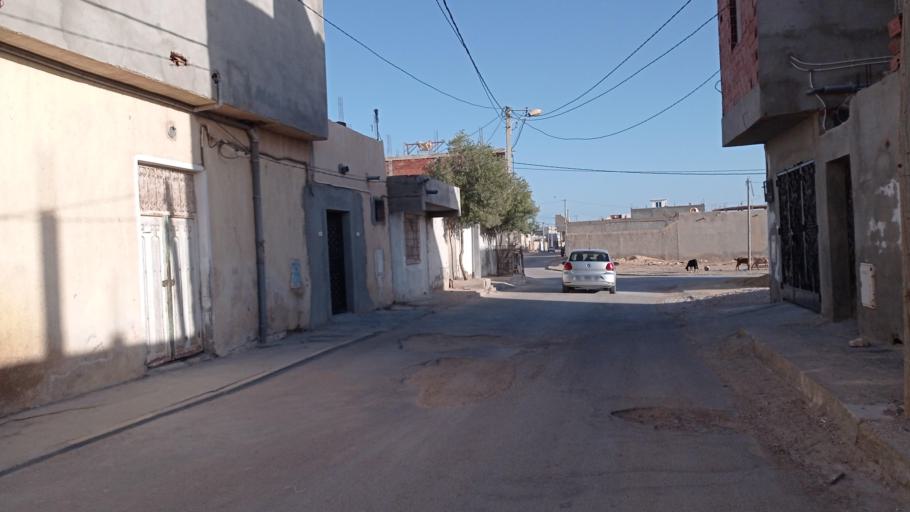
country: TN
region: Qabis
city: Gabes
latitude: 33.8536
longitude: 10.1204
